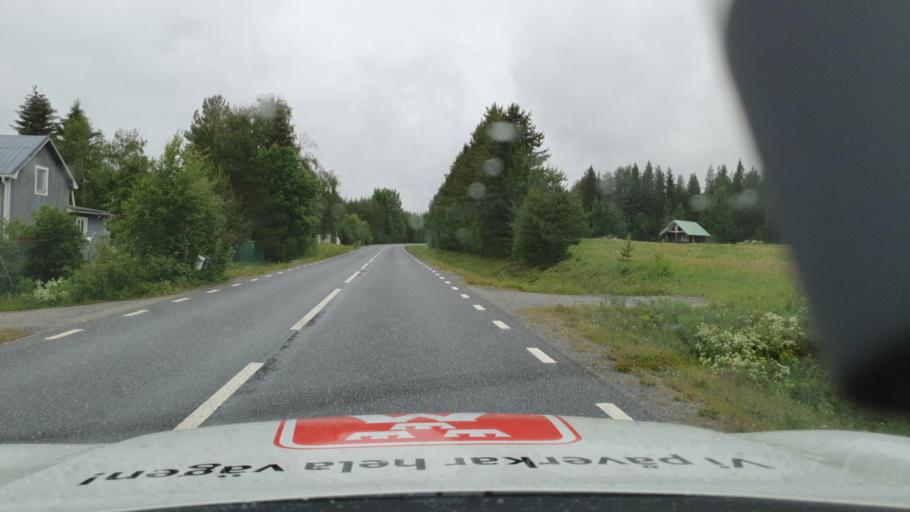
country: SE
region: Vaesterbotten
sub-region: Asele Kommun
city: Asele
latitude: 63.9767
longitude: 17.2639
